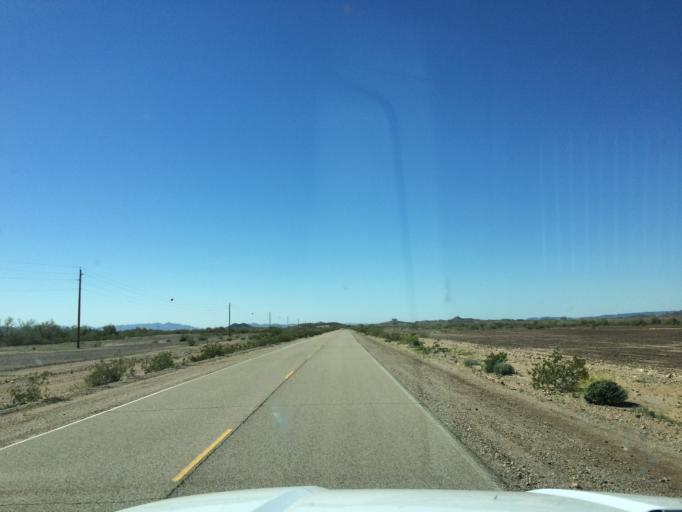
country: US
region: Arizona
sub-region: Yuma County
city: Wellton
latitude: 32.9812
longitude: -114.2725
